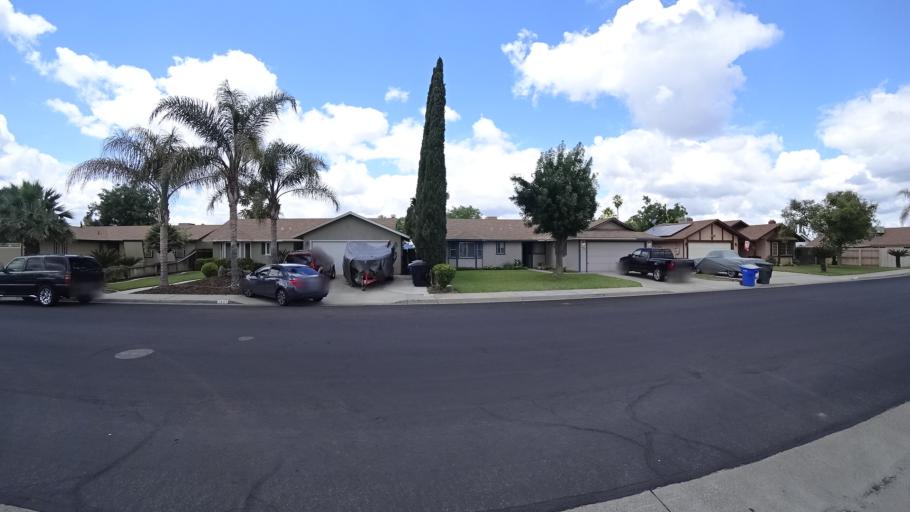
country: US
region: California
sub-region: Kings County
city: Hanford
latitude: 36.3459
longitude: -119.6303
